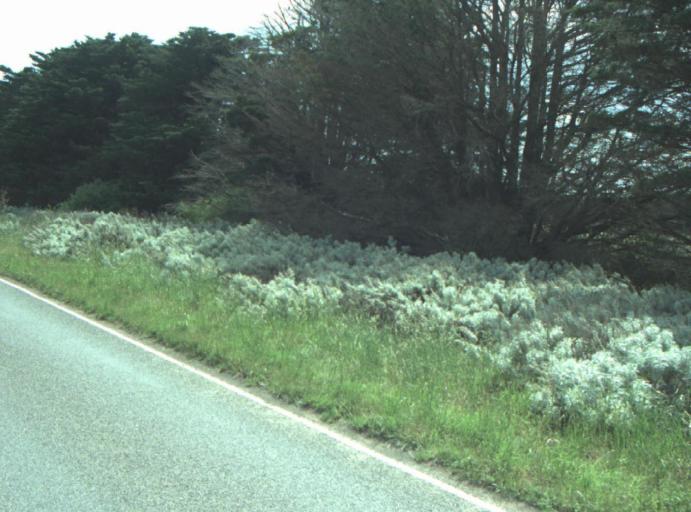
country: AU
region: Victoria
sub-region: Greater Geelong
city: Lara
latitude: -38.0364
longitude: 144.4311
